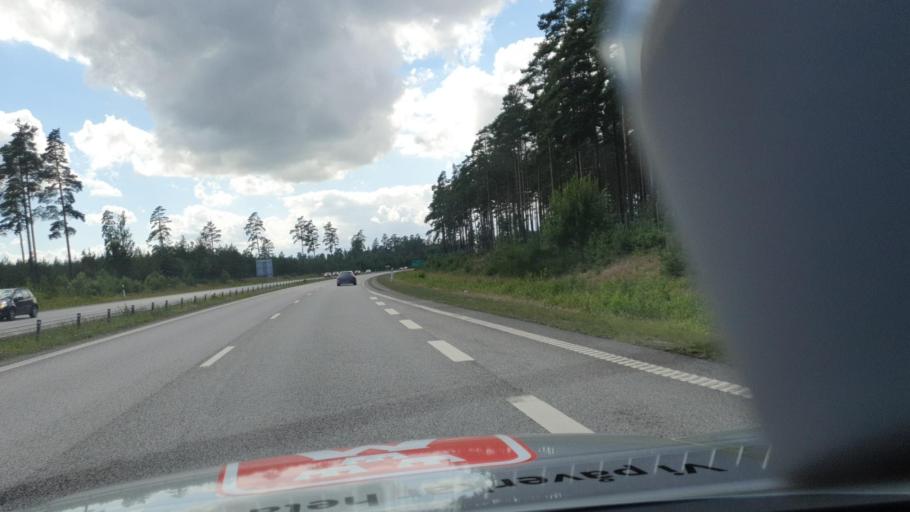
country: SE
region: Skane
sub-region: Bromolla Kommun
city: Bromoella
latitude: 56.0442
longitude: 14.4275
